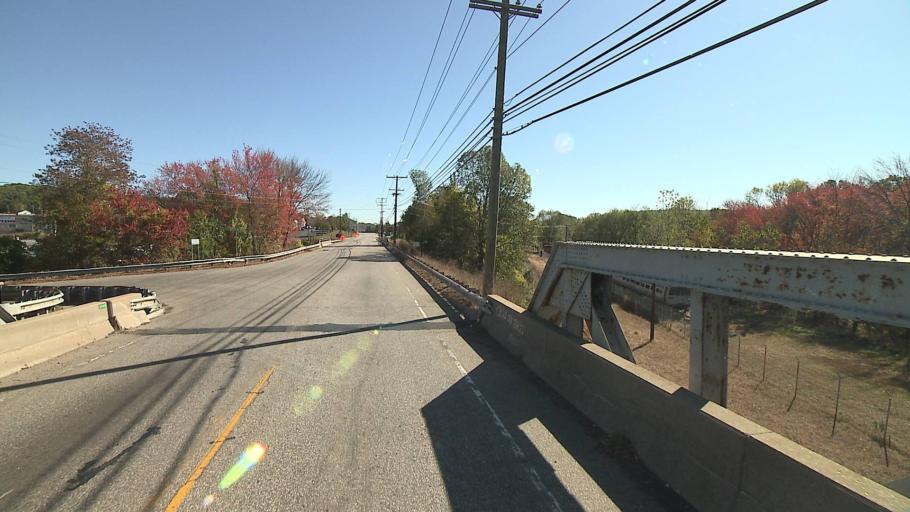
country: US
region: Connecticut
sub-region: Windham County
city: Willimantic
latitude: 41.7167
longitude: -72.2386
